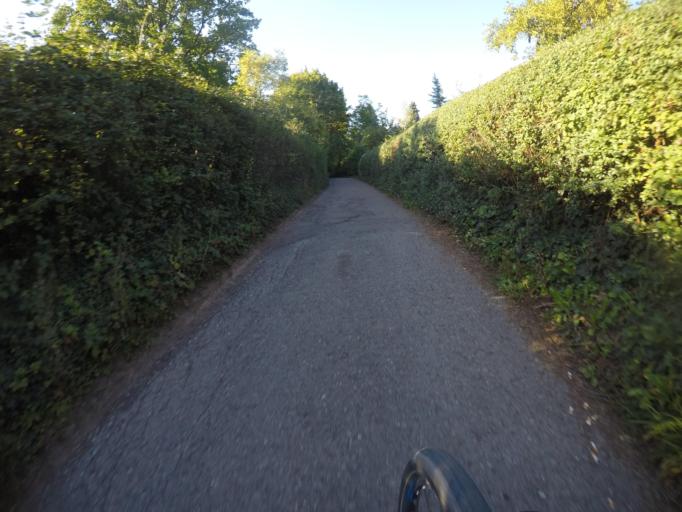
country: DE
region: Baden-Wuerttemberg
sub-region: Regierungsbezirk Stuttgart
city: Stuttgart Feuerbach
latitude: 48.8176
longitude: 9.1523
